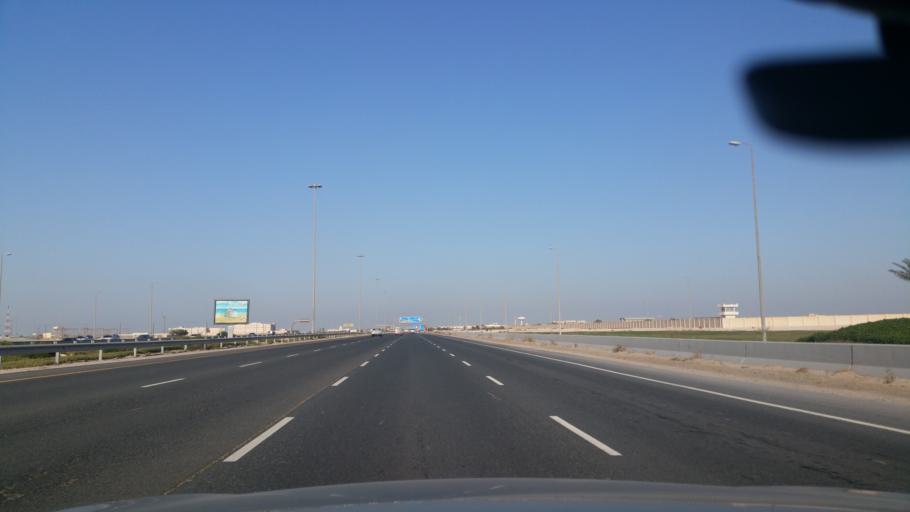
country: QA
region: Baladiyat ar Rayyan
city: Ar Rayyan
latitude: 25.1997
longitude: 51.3870
